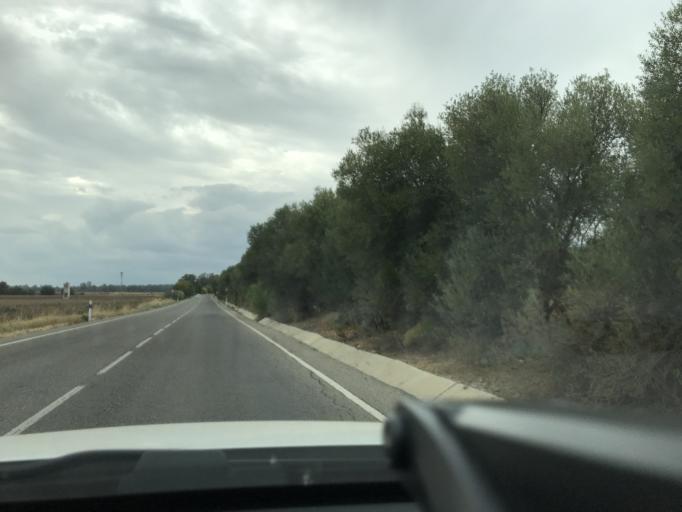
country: ES
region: Andalusia
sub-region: Provincia de Sevilla
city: Villanueva del Rio y Minas
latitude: 37.6353
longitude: -5.7229
